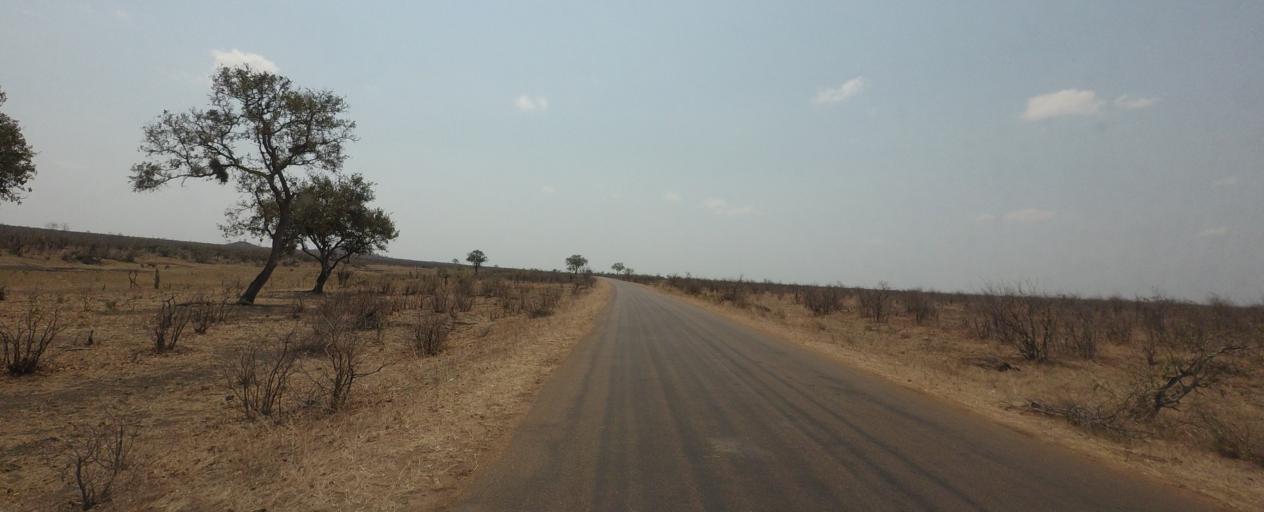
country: ZA
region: Limpopo
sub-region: Mopani District Municipality
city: Phalaborwa
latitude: -23.5053
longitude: 31.4048
